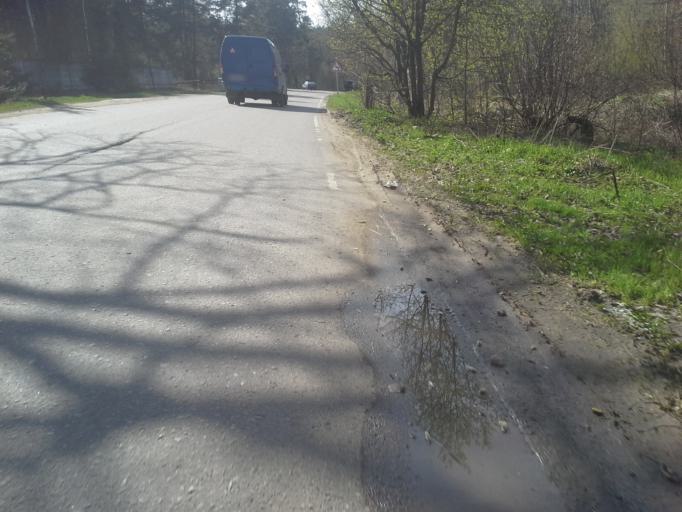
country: RU
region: Moskovskaya
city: Dubrovitsy
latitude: 55.4420
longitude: 37.4705
